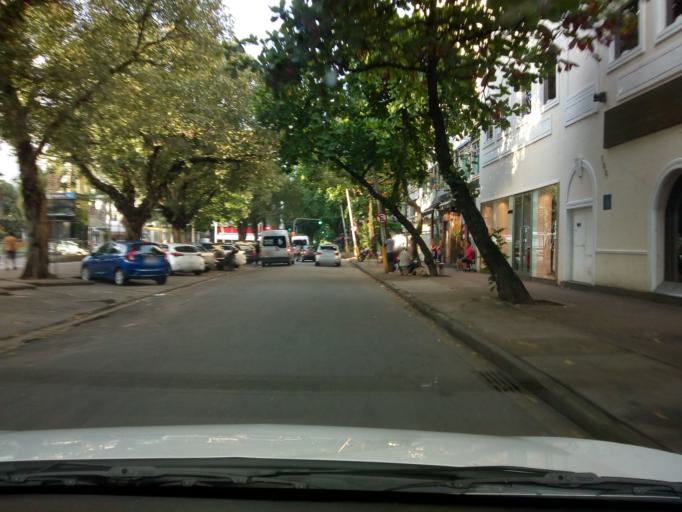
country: BR
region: Rio de Janeiro
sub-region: Rio De Janeiro
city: Rio de Janeiro
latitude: -22.9841
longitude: -43.2048
